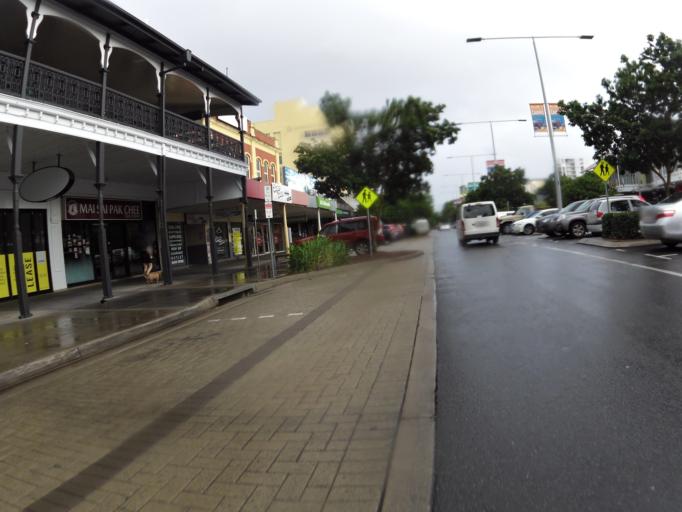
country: AU
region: Queensland
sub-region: Cairns
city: Cairns
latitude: -16.9236
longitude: 145.7770
